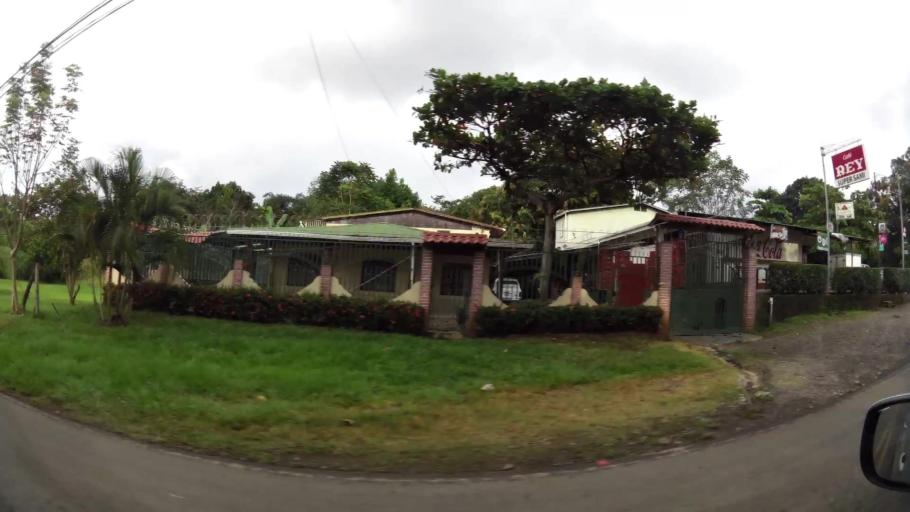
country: CR
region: Puntarenas
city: Esparza
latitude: 9.9758
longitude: -84.6190
